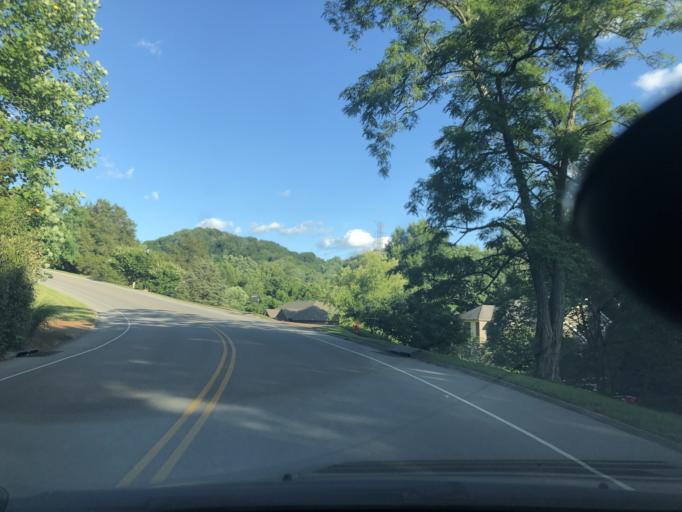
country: US
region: Tennessee
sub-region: Davidson County
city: Forest Hills
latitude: 36.0575
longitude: -86.8318
